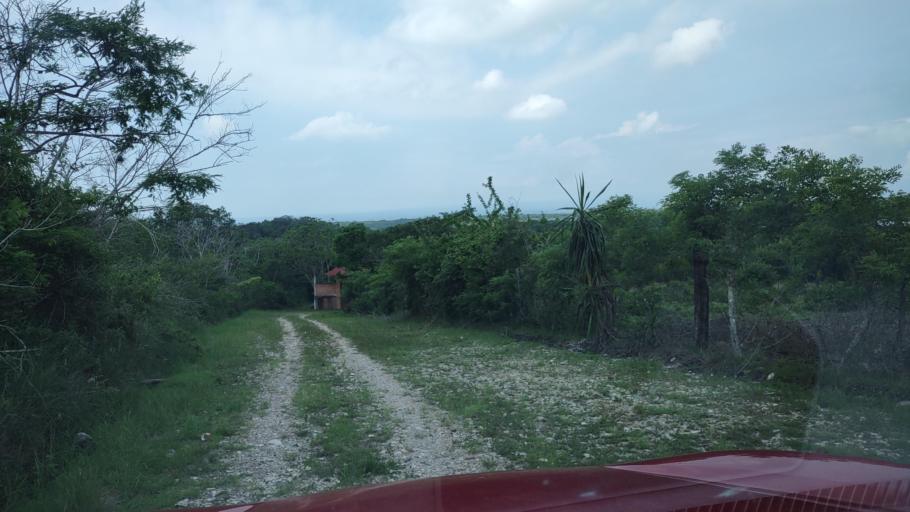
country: MX
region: Veracruz
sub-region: Emiliano Zapata
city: Dos Rios
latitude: 19.4488
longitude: -96.8094
